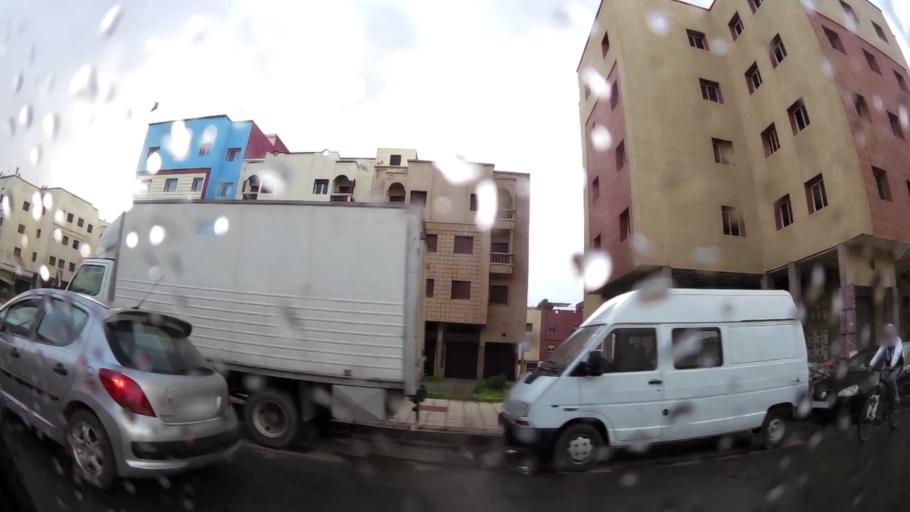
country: MA
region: Grand Casablanca
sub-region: Mohammedia
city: Mohammedia
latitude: 33.6791
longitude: -7.3862
